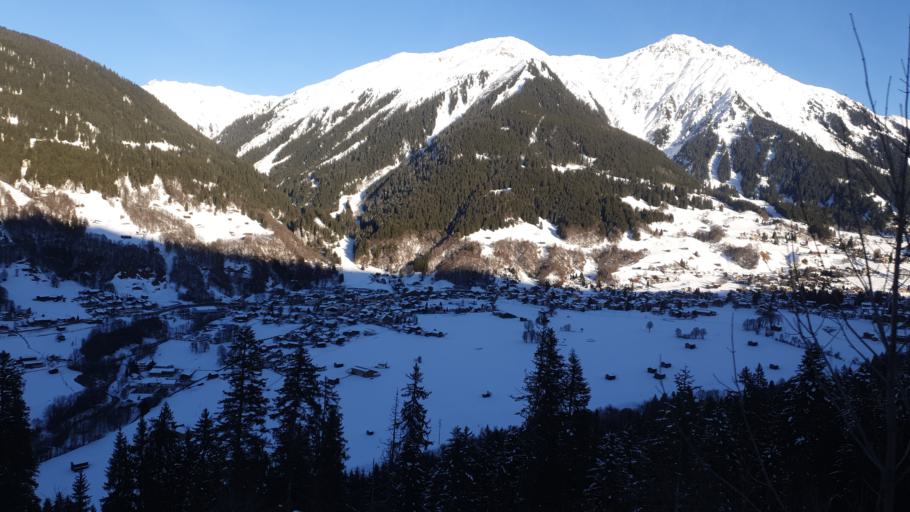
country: CH
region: Grisons
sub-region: Praettigau/Davos District
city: Klosters Serneus
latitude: 46.8752
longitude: 9.8595
